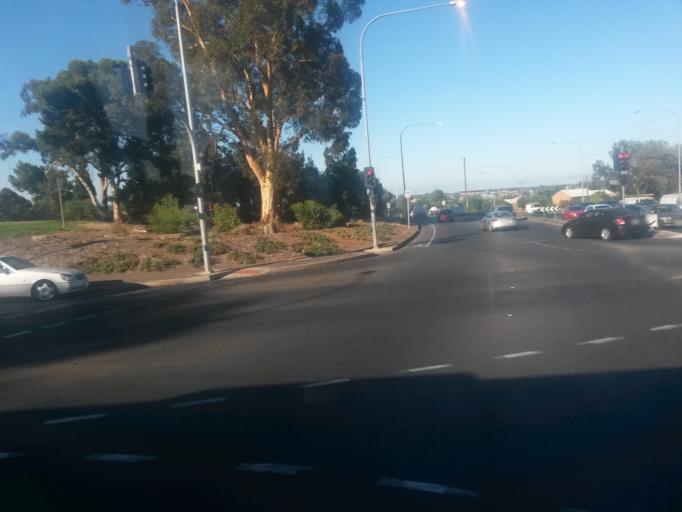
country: AU
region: South Australia
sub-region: Adelaide
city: North Adelaide
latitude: -34.8994
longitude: 138.5883
